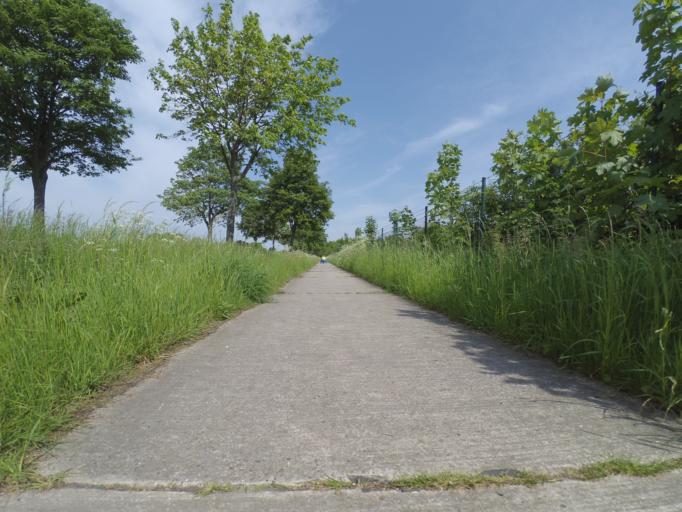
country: DE
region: Lower Saxony
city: Hohenhameln
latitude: 52.2627
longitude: 10.0517
